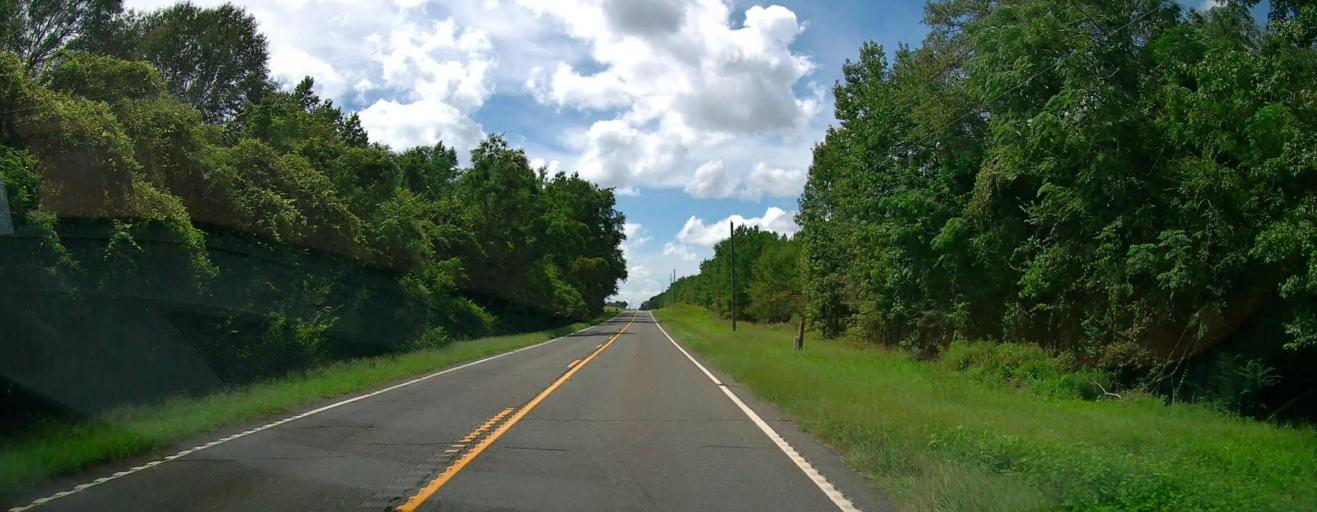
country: US
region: Georgia
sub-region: Macon County
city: Marshallville
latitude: 32.4335
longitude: -84.0548
